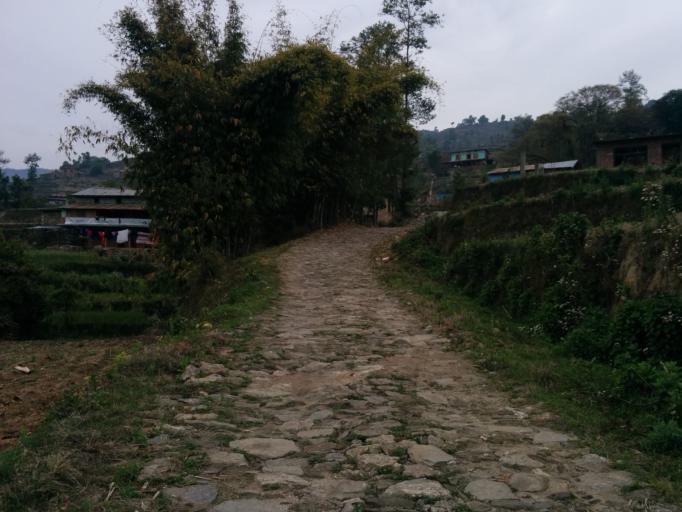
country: NP
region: Central Region
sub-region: Bagmati Zone
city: Bhaktapur
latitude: 27.7759
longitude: 85.4296
